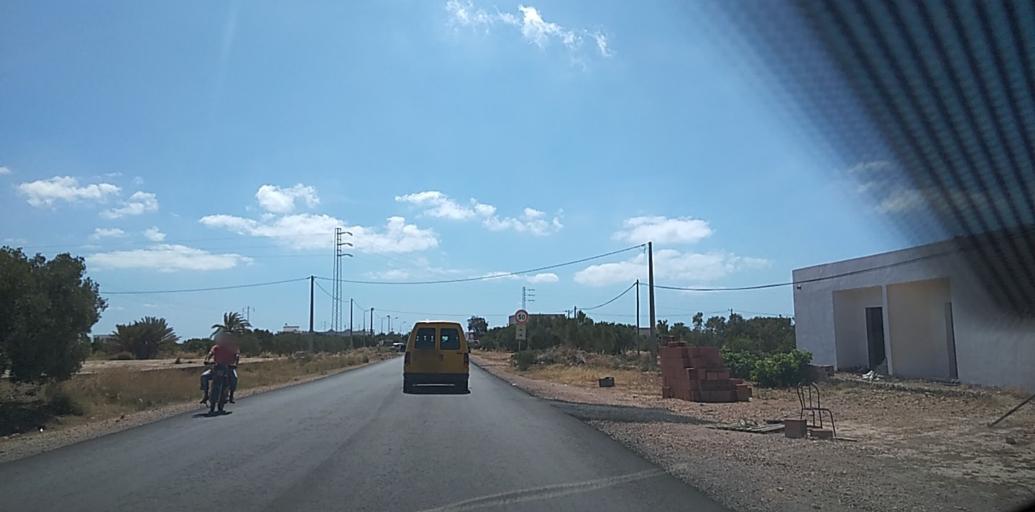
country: TN
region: Safaqis
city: Al Qarmadah
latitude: 34.6570
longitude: 11.0863
